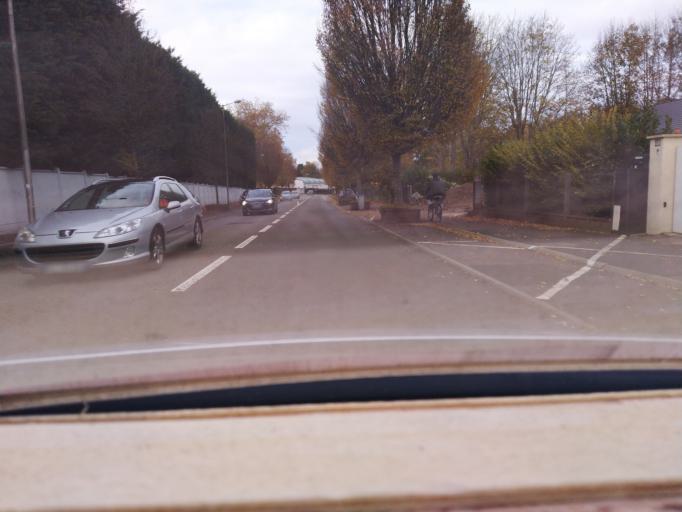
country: FR
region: Haute-Normandie
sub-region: Departement de la Seine-Maritime
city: Canteleu
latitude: 49.4425
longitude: 1.0212
